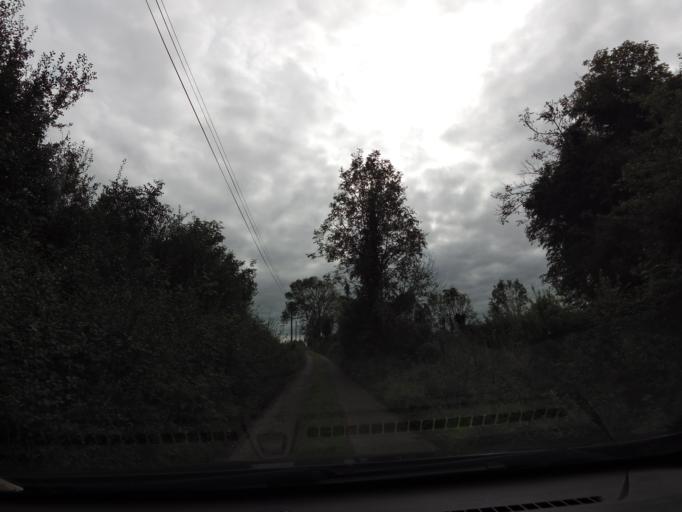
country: IE
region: Connaught
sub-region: County Galway
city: Loughrea
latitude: 53.1623
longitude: -8.4380
